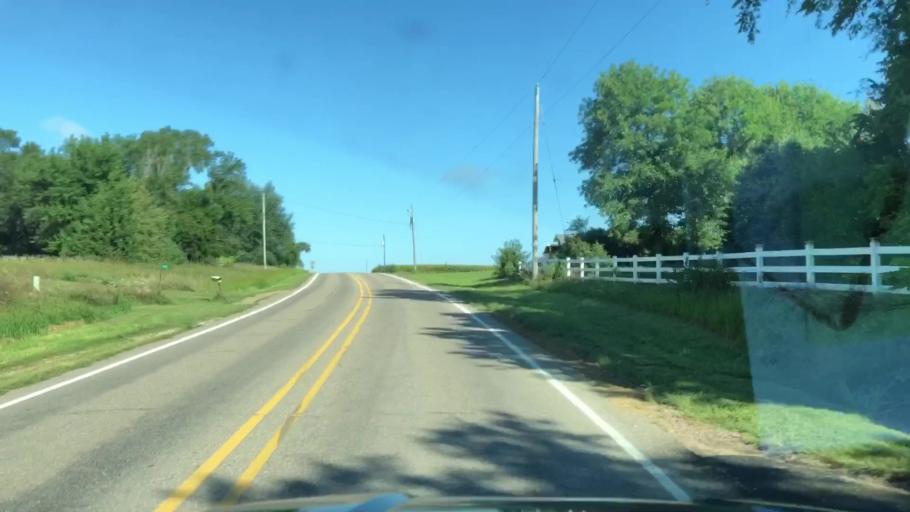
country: US
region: Iowa
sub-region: Woodbury County
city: Sergeant Bluff
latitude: 42.4252
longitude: -96.2775
